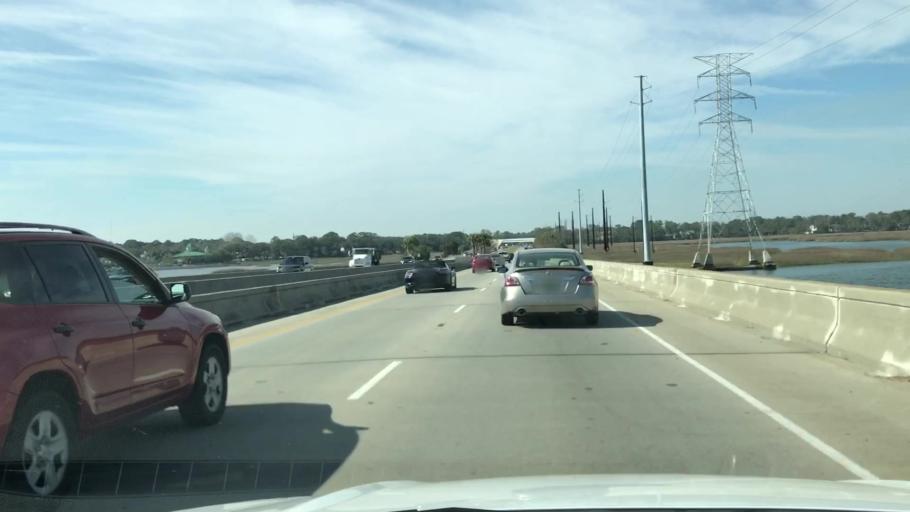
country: US
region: South Carolina
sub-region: Beaufort County
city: Hilton Head Island
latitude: 32.2308
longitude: -80.7922
